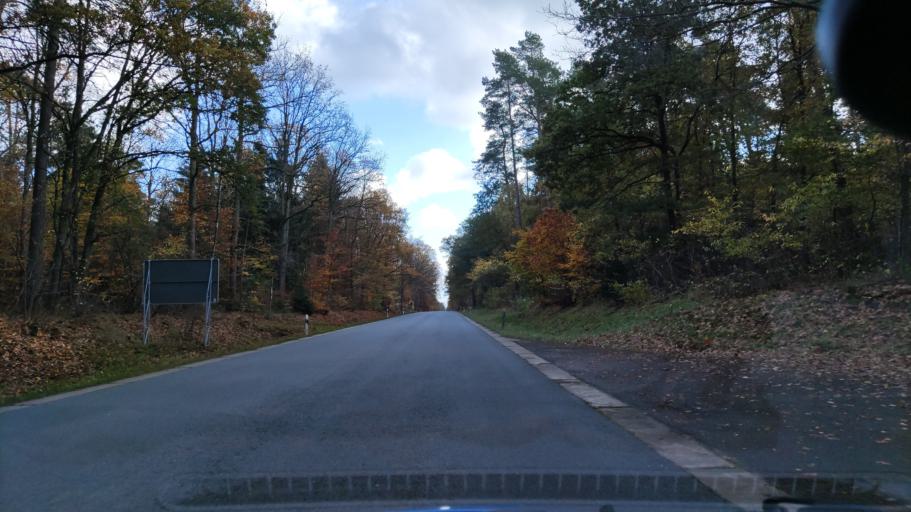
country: DE
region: Lower Saxony
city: Munster
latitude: 53.0117
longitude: 10.1007
